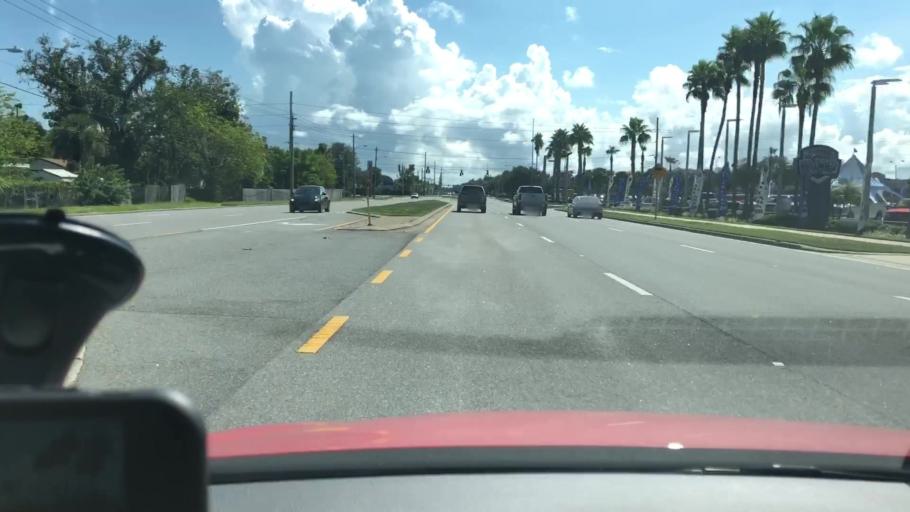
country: US
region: Florida
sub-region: Volusia County
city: Daytona Beach
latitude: 29.2084
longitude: -81.0425
